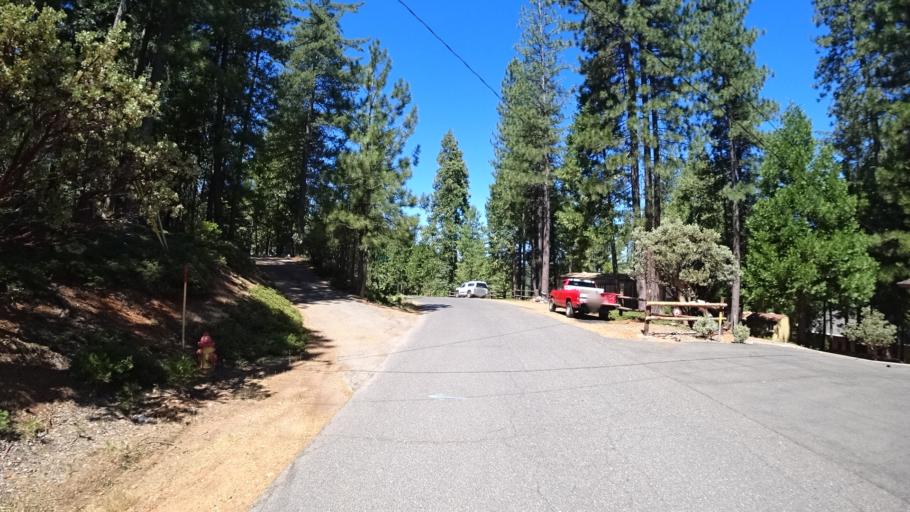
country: US
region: California
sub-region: Calaveras County
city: Arnold
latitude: 38.2303
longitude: -120.3422
